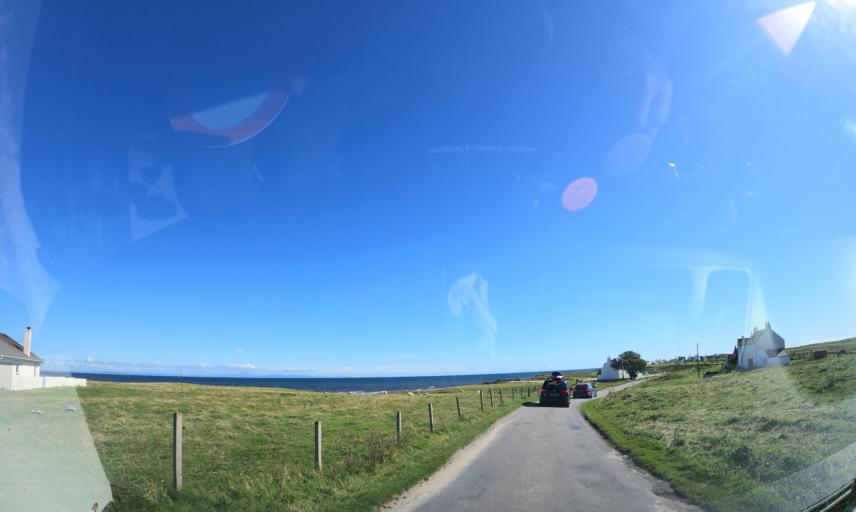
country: GB
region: Scotland
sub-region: Eilean Siar
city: Barra
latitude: 56.4721
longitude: -6.8997
